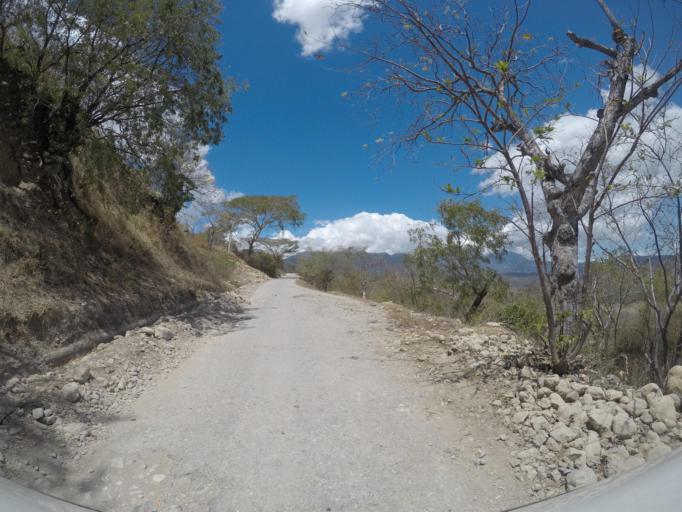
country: TL
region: Baucau
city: Baucau
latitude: -8.4832
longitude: 126.6088
